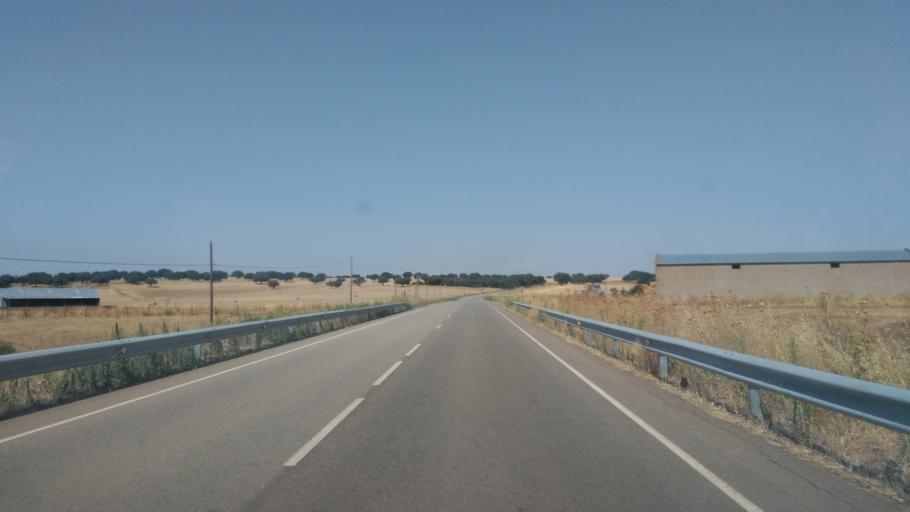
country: ES
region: Castille and Leon
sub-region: Provincia de Salamanca
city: Cabrillas
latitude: 40.7449
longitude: -6.1803
